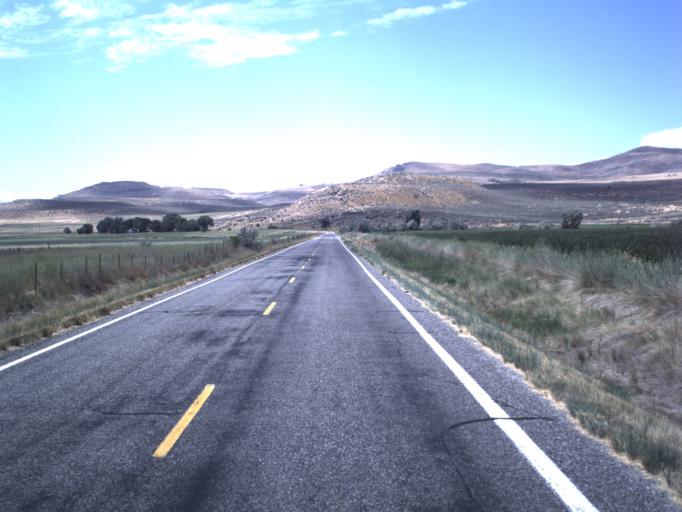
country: US
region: Utah
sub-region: Box Elder County
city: Tremonton
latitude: 41.6369
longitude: -112.3181
